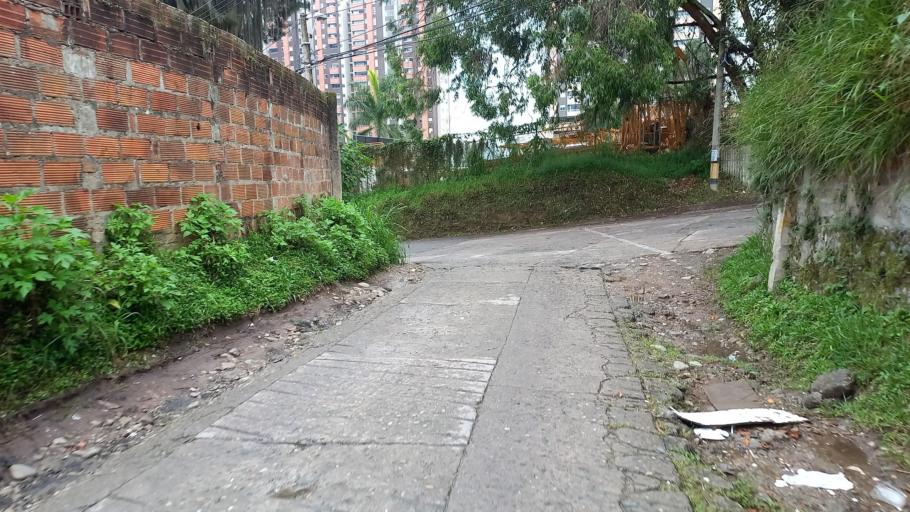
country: CO
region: Antioquia
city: La Estrella
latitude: 6.1659
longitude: -75.6476
